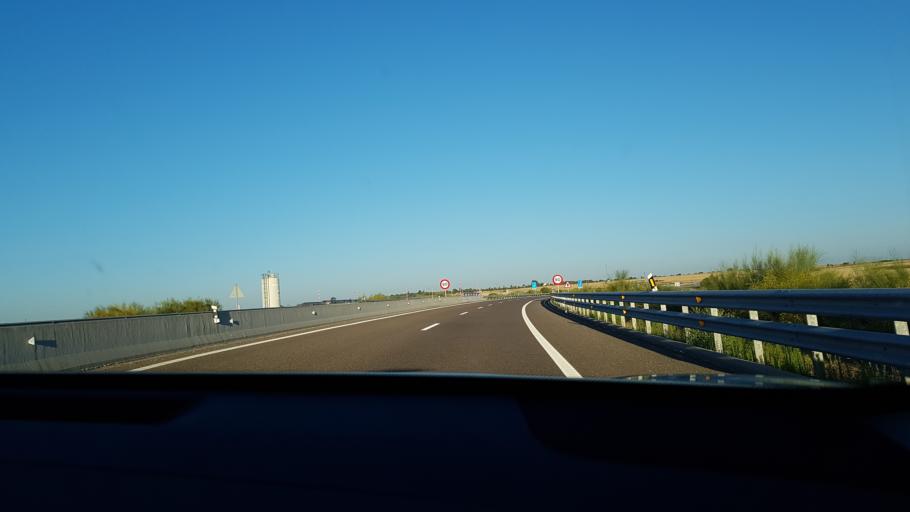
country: ES
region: Castille and Leon
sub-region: Provincia de Zamora
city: Roales
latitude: 41.5237
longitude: -5.7977
